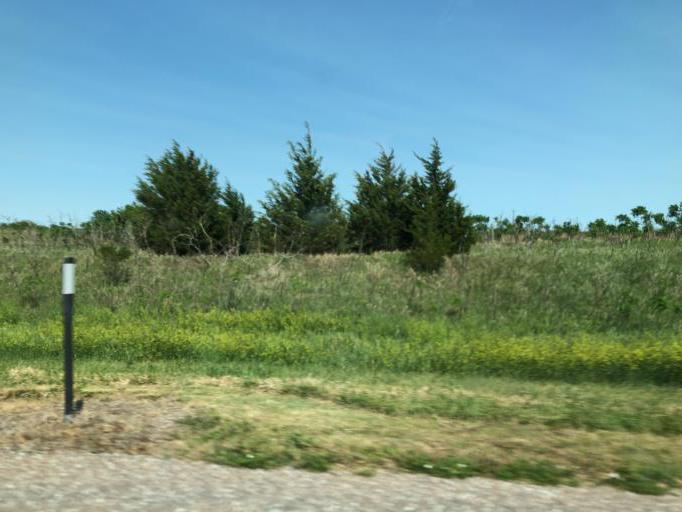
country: US
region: Nebraska
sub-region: Fillmore County
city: Geneva
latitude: 40.3807
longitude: -97.5772
